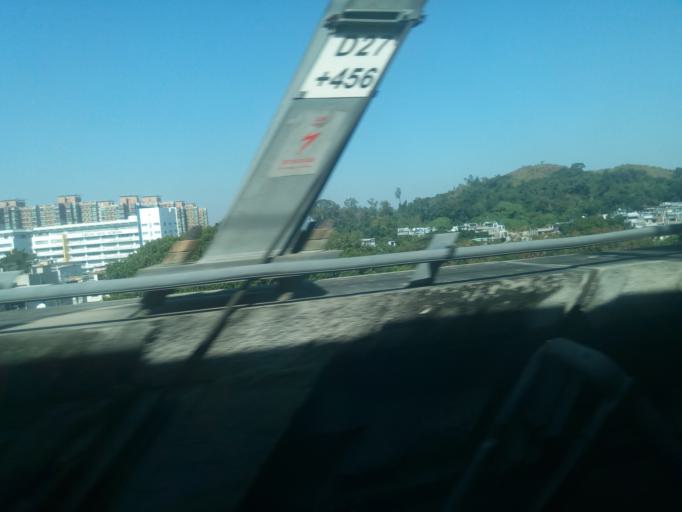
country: HK
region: Yuen Long
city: Yuen Long Kau Hui
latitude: 22.4463
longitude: 114.0334
